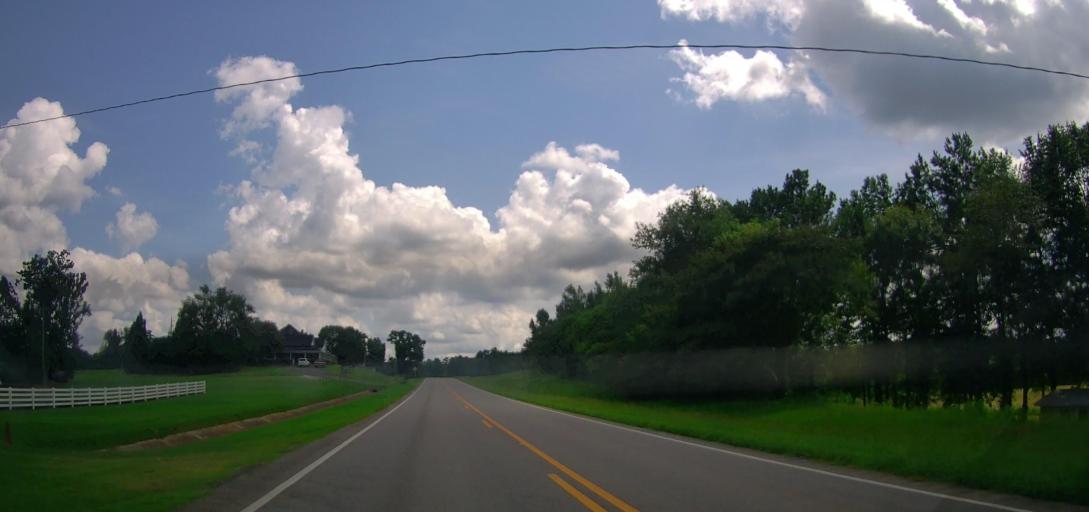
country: US
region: Alabama
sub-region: Cleburne County
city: Heflin
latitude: 33.6162
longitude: -85.4741
